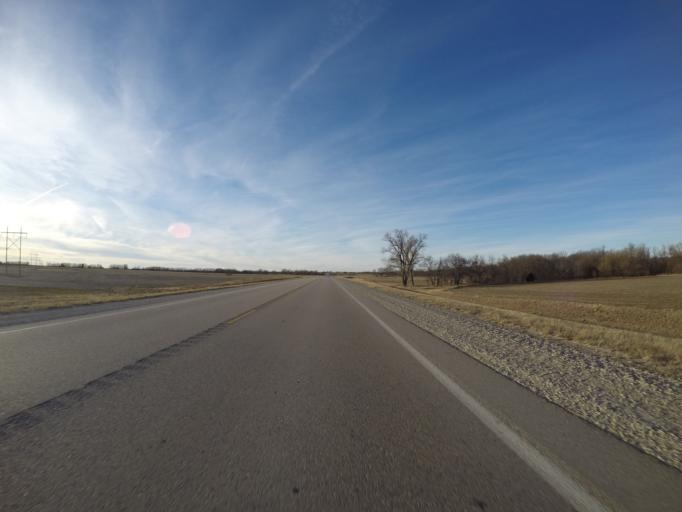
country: US
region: Kansas
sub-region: Marion County
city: Marion
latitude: 38.2539
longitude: -96.9529
